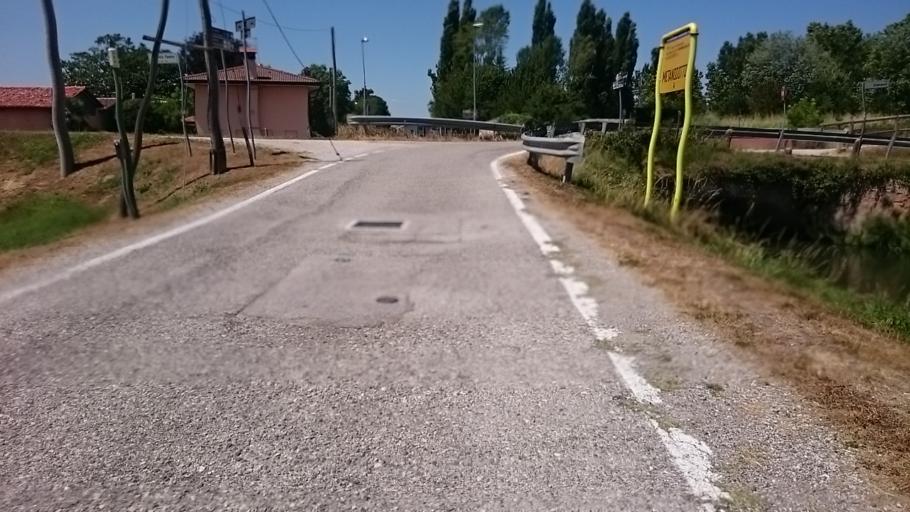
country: IT
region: Veneto
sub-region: Provincia di Padova
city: Borgoricco-San Michele delle Badesse-Sant'Eufemia
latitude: 45.5273
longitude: 11.9214
